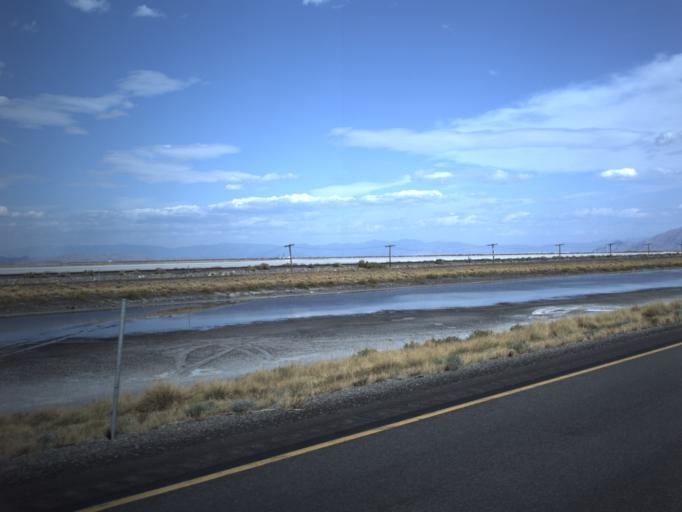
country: US
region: Utah
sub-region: Tooele County
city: Grantsville
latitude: 40.7203
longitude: -112.5563
